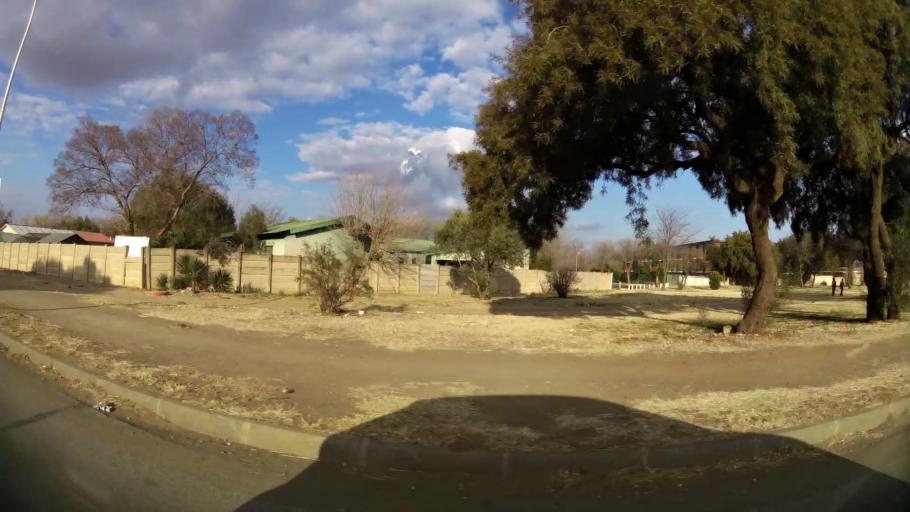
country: ZA
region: Orange Free State
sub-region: Mangaung Metropolitan Municipality
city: Bloemfontein
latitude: -29.0988
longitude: 26.1881
